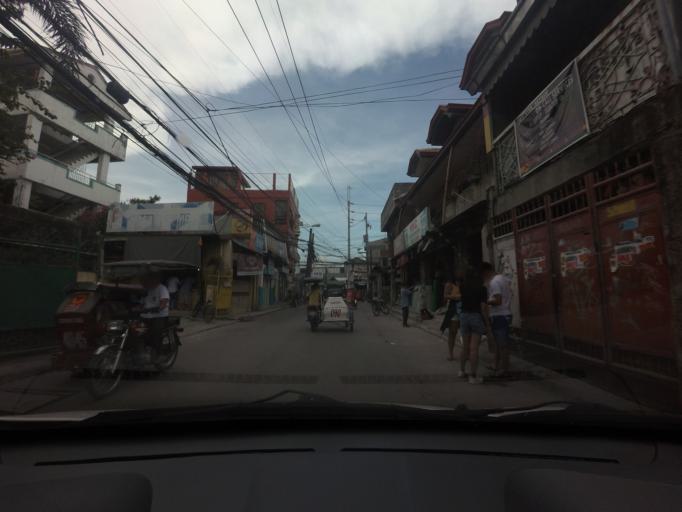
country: PH
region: Calabarzon
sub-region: Province of Rizal
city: Pateros
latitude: 14.5377
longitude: 121.0598
